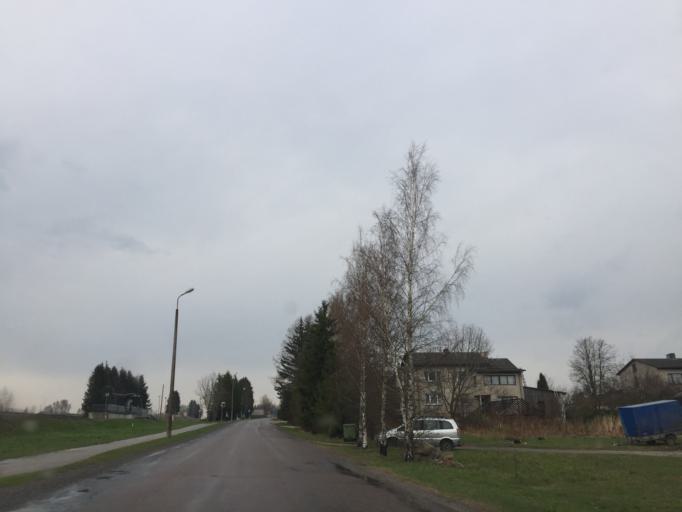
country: EE
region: Tartu
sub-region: UElenurme vald
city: Ulenurme
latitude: 58.3087
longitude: 26.7222
